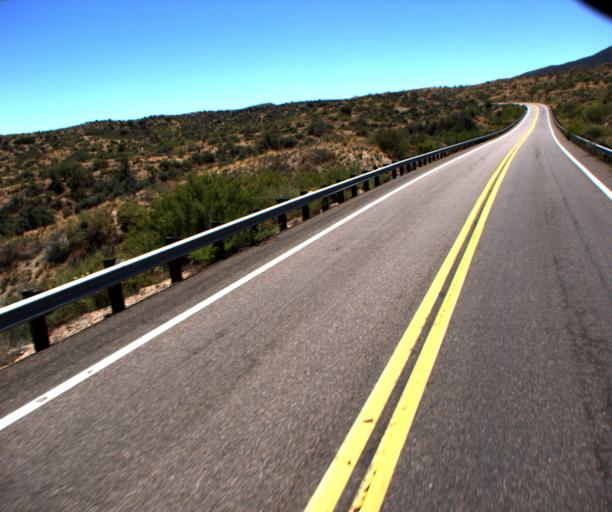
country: US
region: Arizona
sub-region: Gila County
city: Globe
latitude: 33.3306
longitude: -110.7305
